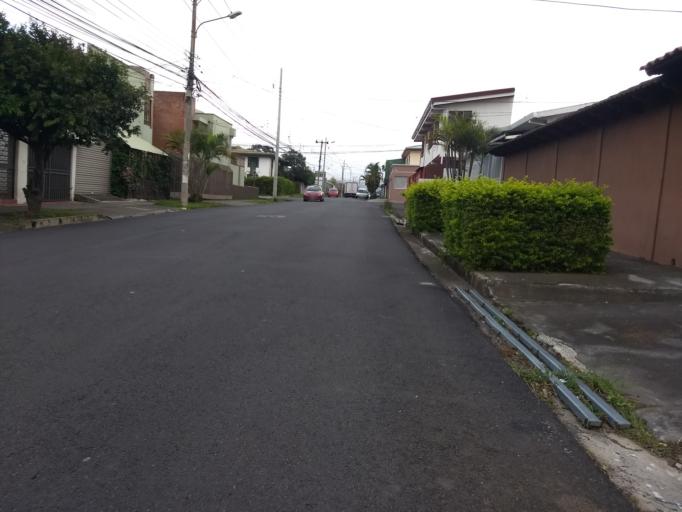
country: CR
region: San Jose
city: San Juan
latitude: 9.9555
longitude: -84.0811
